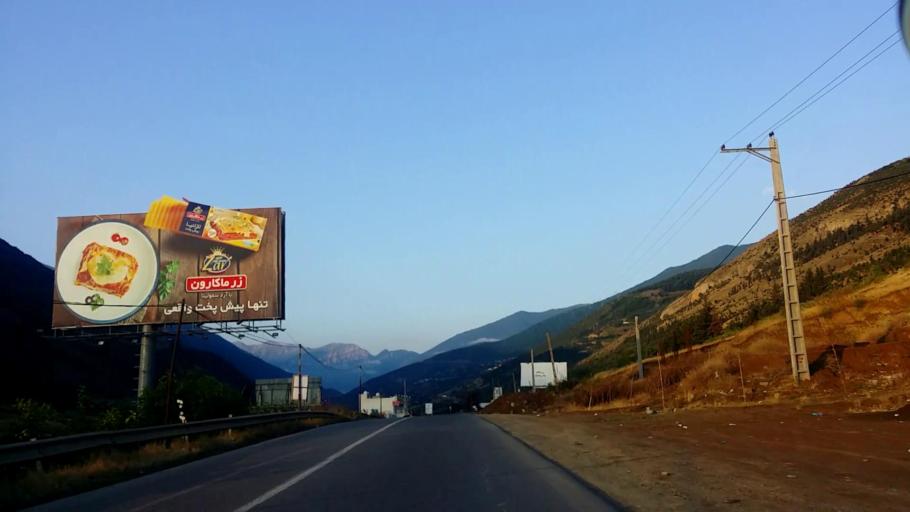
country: IR
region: Mazandaran
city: Chalus
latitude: 36.4401
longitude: 51.2922
